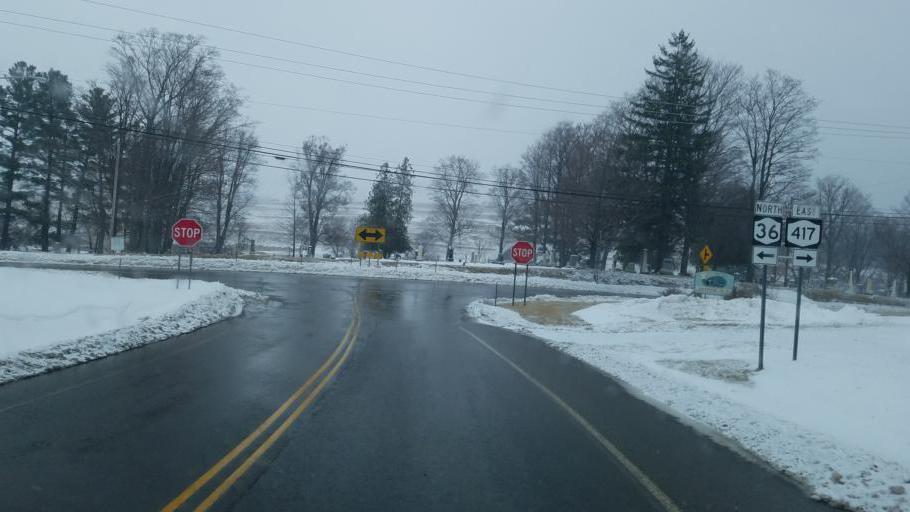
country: US
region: New York
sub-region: Steuben County
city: Canisteo
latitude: 42.1253
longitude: -77.5080
